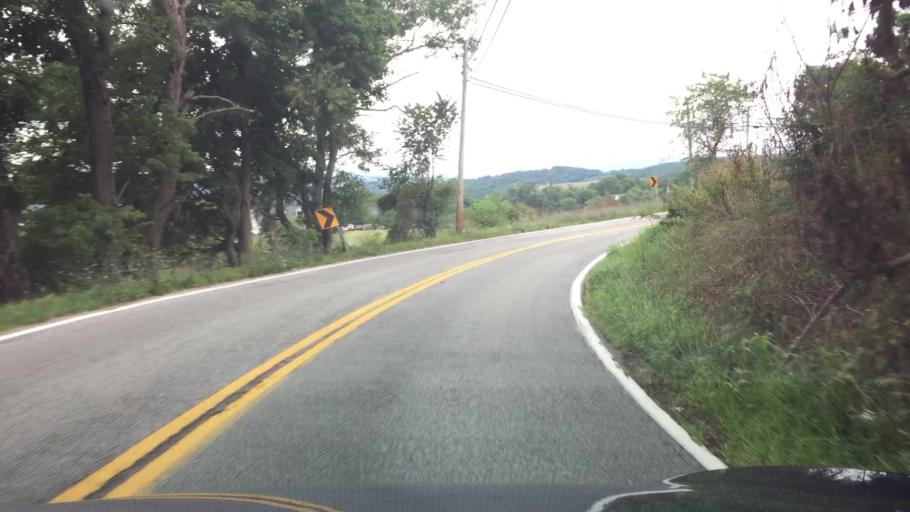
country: US
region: Virginia
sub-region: Pulaski County
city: Pulaski
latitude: 37.0084
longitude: -80.7434
